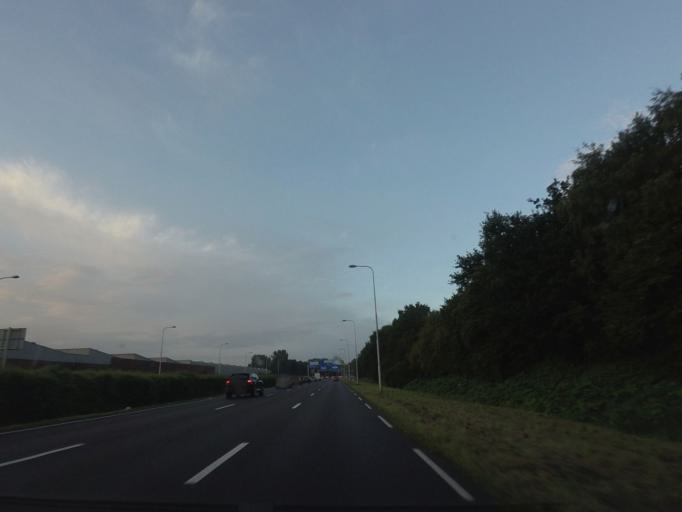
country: NL
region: North Holland
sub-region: Gemeente Alkmaar
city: Alkmaar
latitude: 52.6527
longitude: 4.7664
